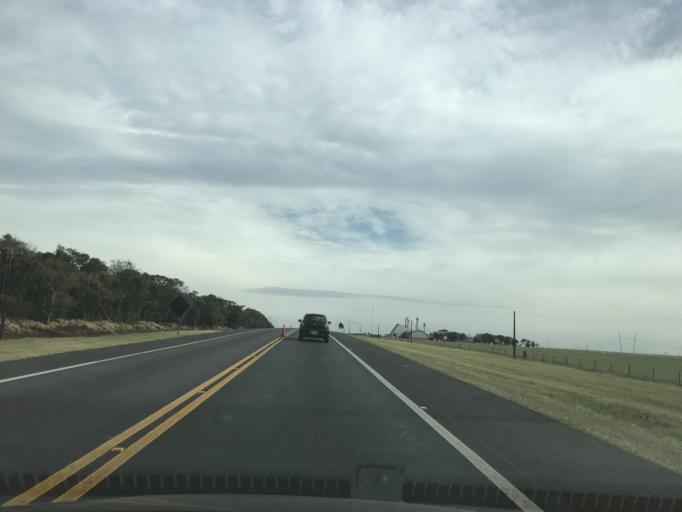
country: BR
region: Parana
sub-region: Cascavel
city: Cascavel
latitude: -25.0758
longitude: -53.6929
